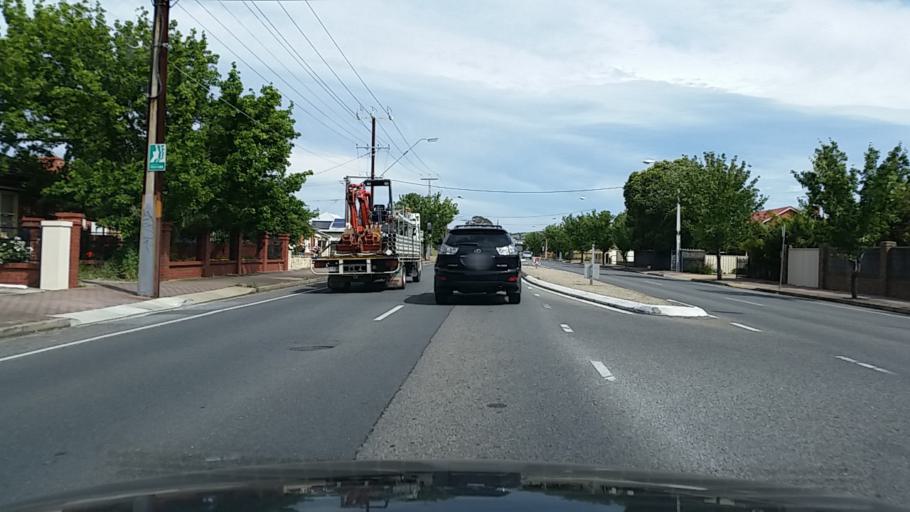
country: AU
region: South Australia
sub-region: Holdfast Bay
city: North Brighton
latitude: -35.0014
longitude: 138.5338
